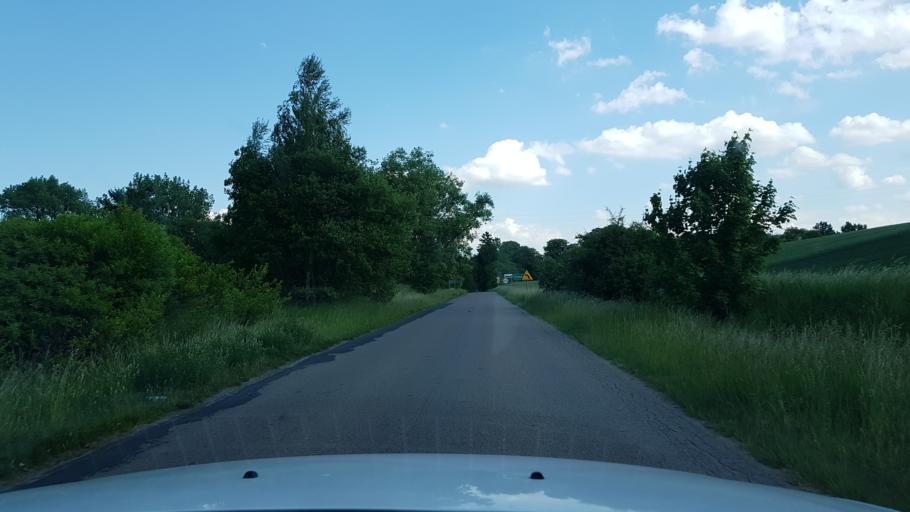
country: PL
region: West Pomeranian Voivodeship
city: Trzcinsko Zdroj
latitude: 53.0339
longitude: 14.6177
